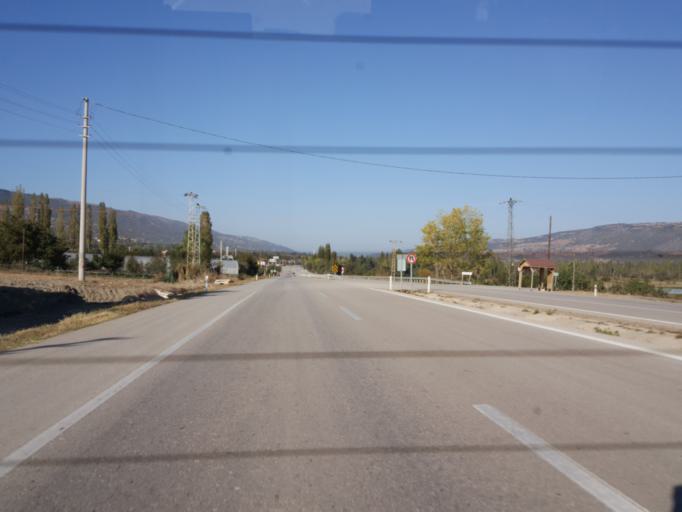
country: TR
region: Amasya
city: Ezinepazari
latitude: 40.5687
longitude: 36.0767
